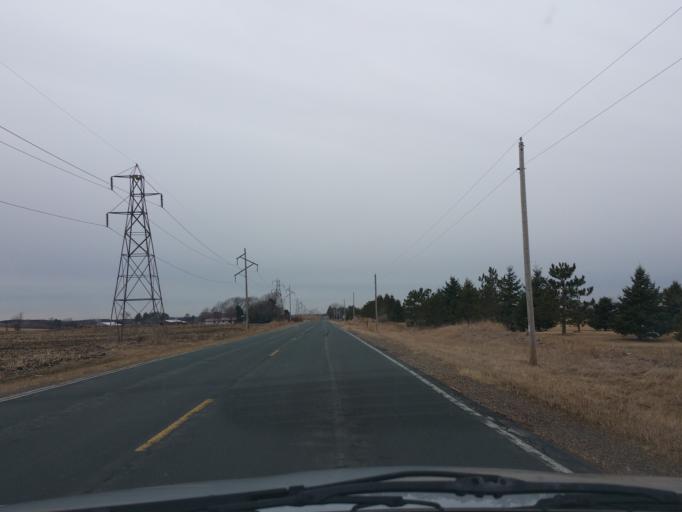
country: US
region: Wisconsin
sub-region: Saint Croix County
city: Roberts
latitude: 45.0357
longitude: -92.5604
